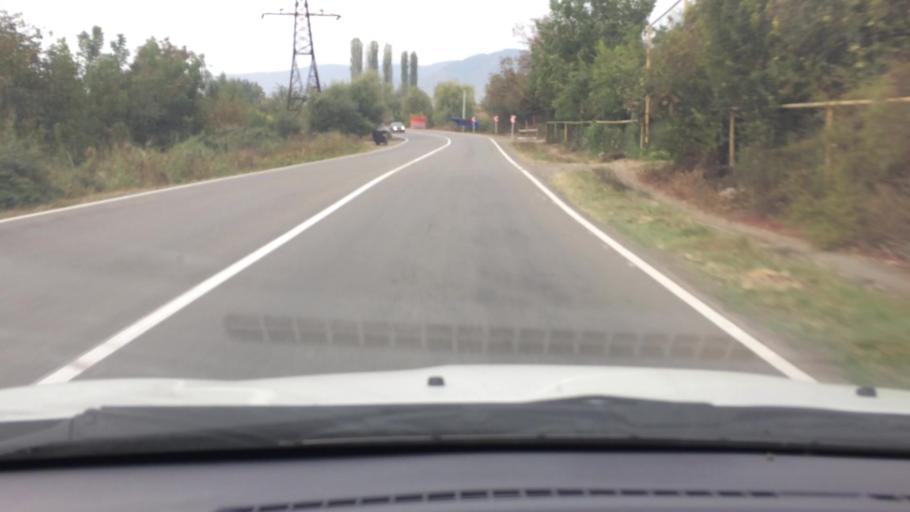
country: GE
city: Naghvarevi
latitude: 41.3231
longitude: 44.7989
